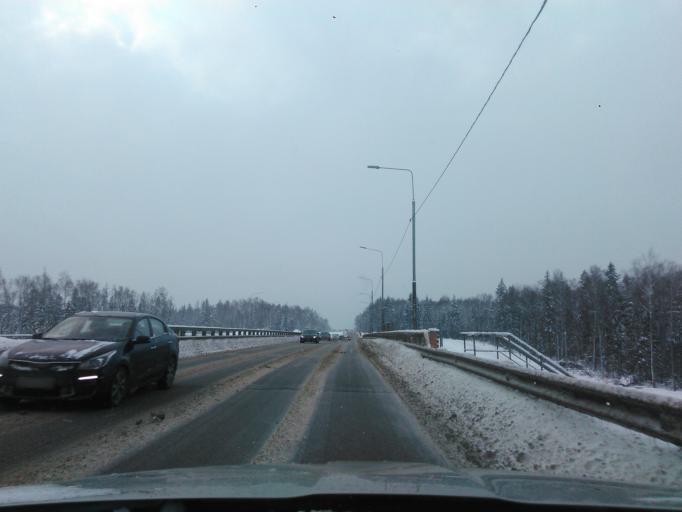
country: RU
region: Moskovskaya
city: Povarovo
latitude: 56.0292
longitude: 37.0603
